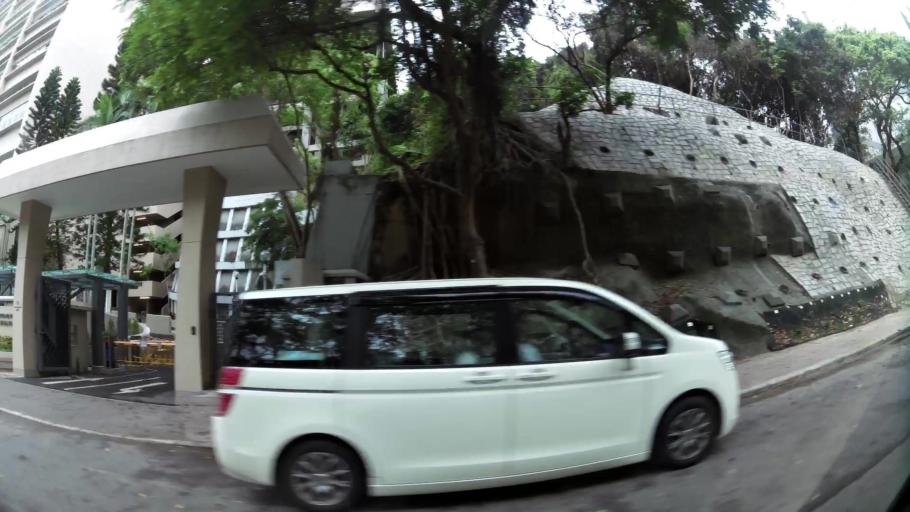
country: HK
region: Central and Western
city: Central
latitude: 22.2505
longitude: 114.1587
